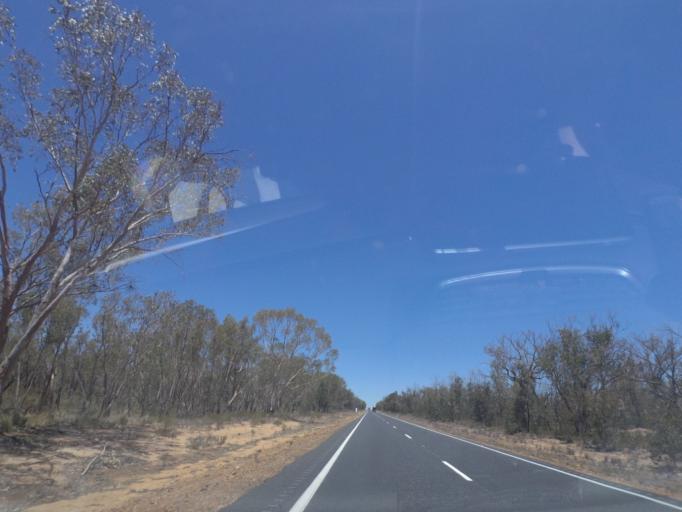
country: AU
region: New South Wales
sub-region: Warrumbungle Shire
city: Coonabarabran
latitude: -30.9555
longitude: 149.4206
